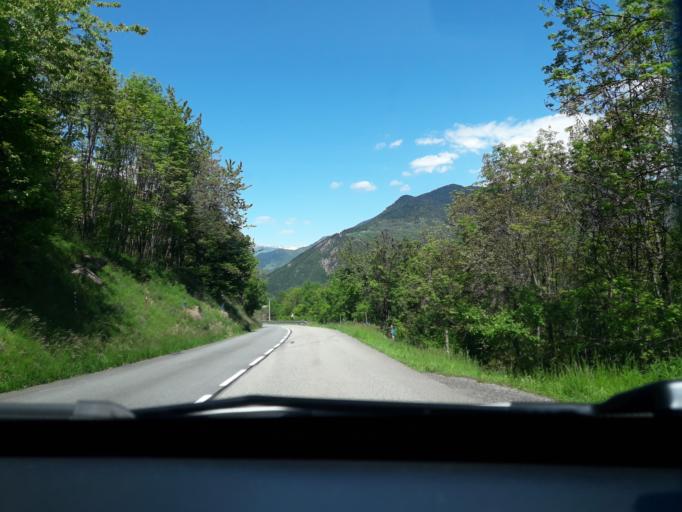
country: FR
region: Rhone-Alpes
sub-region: Departement de la Savoie
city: Salins-les-Thermes
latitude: 45.4539
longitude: 6.5075
